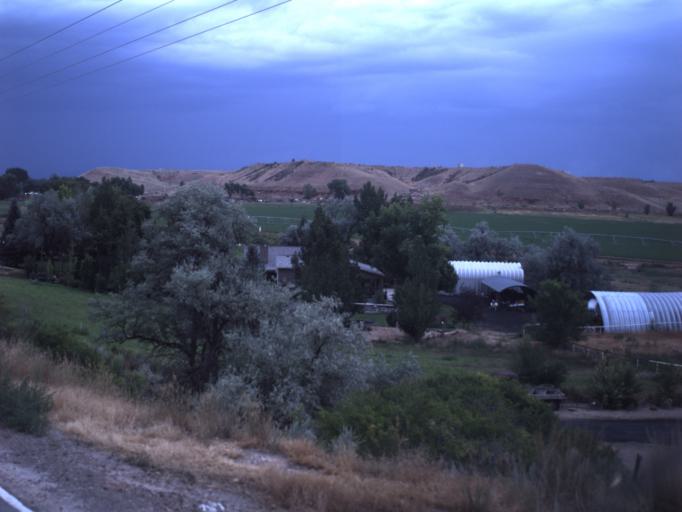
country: US
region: Utah
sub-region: Duchesne County
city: Roosevelt
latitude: 40.3092
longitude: -110.0078
